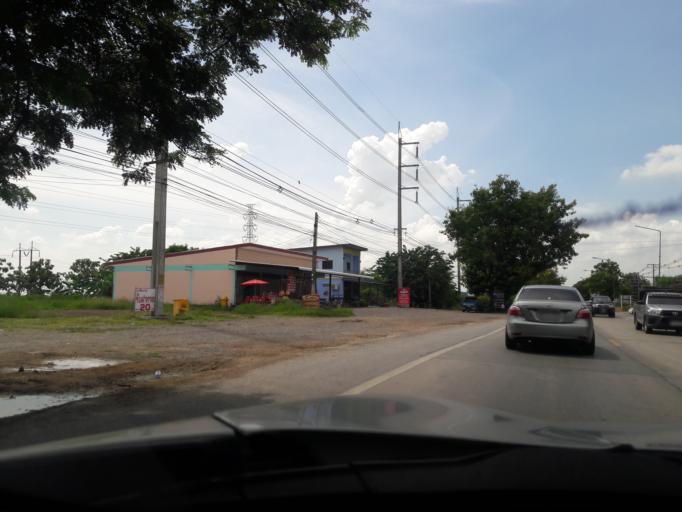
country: TH
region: Phra Nakhon Si Ayutthaya
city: Maha Rat
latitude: 14.5784
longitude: 100.5283
